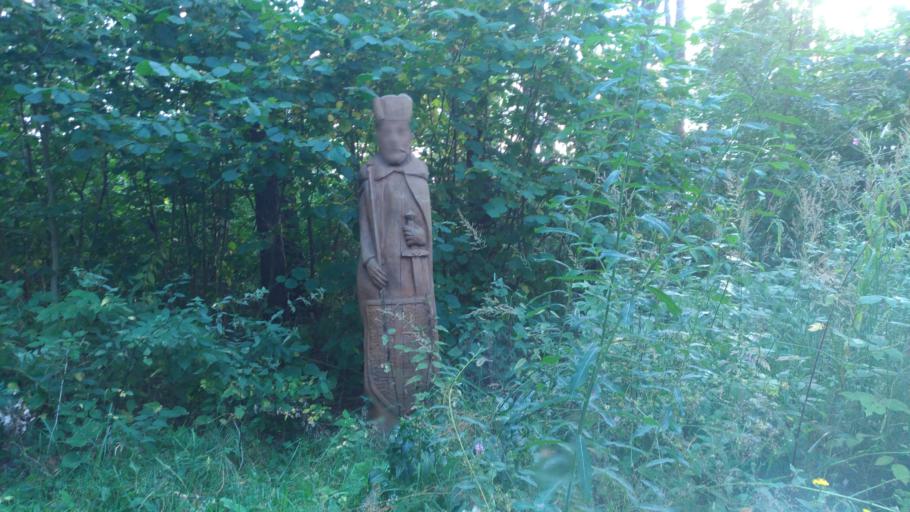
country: LT
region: Vilnius County
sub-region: Trakai
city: Rudiskes
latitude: 54.6253
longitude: 24.8230
